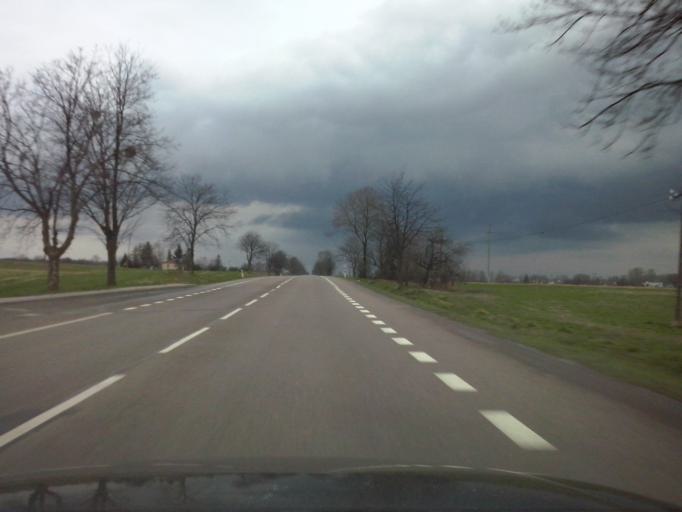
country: PL
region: Lublin Voivodeship
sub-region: Powiat chelmski
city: Rejowiec Fabryczny
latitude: 51.1757
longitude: 23.2473
